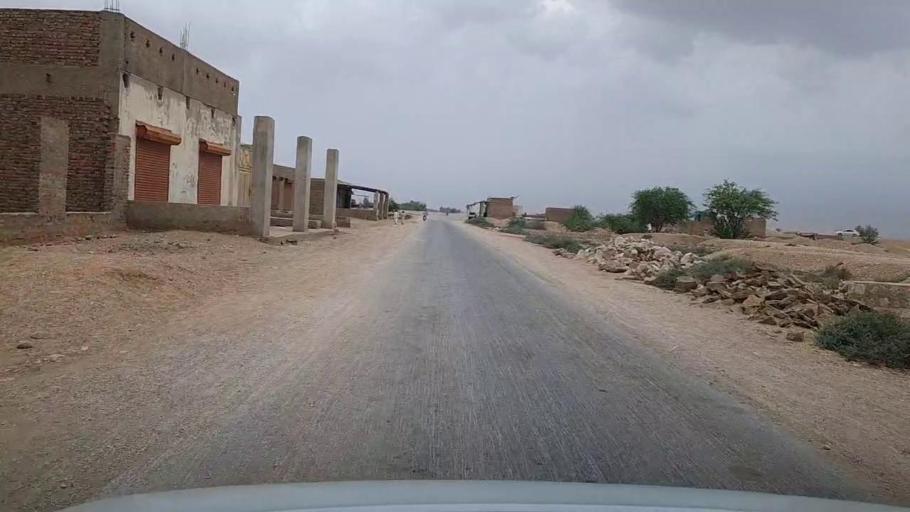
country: PK
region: Sindh
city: Sehwan
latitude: 26.3356
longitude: 67.7234
